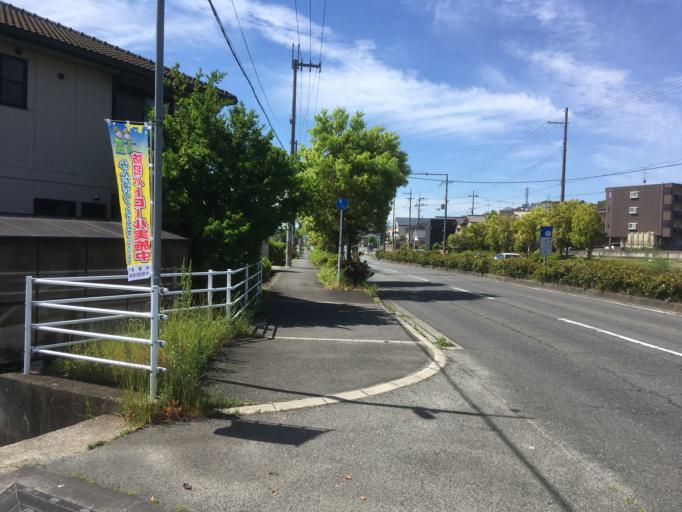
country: JP
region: Nara
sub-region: Ikoma-shi
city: Ikoma
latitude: 34.6781
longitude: 135.7063
